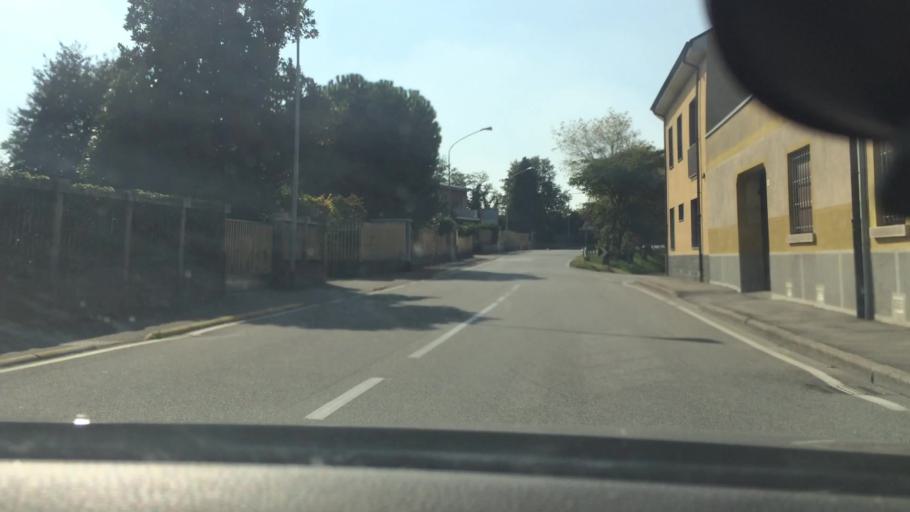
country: IT
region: Lombardy
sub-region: Citta metropolitana di Milano
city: Busto Garolfo
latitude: 45.5426
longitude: 8.8795
